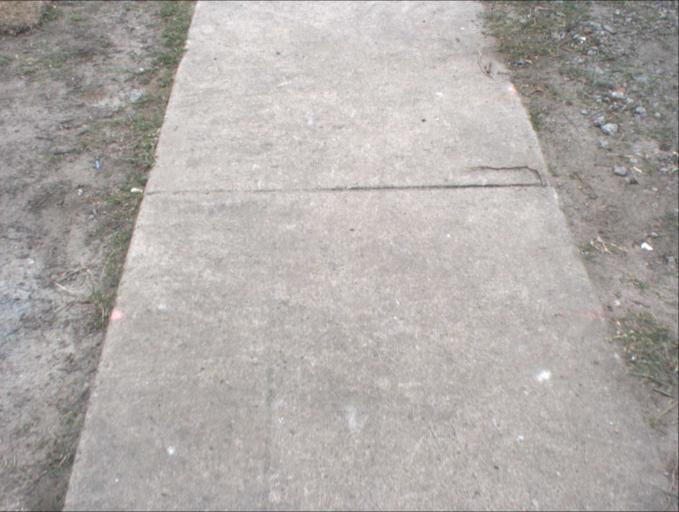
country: AU
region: Queensland
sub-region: Logan
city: Park Ridge South
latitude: -27.6769
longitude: 153.0448
